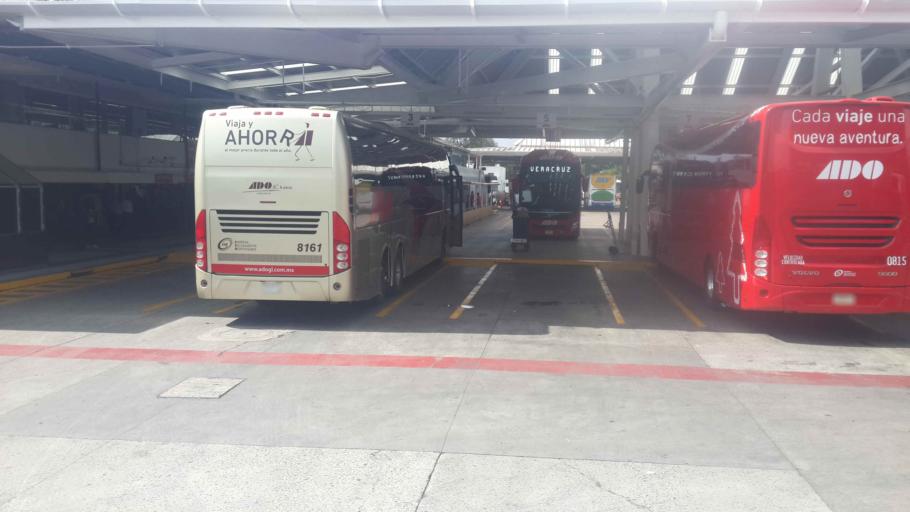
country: MX
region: Veracruz
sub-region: Xalapa
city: Xalapa de Enriquez
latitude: 19.5277
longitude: -96.9029
